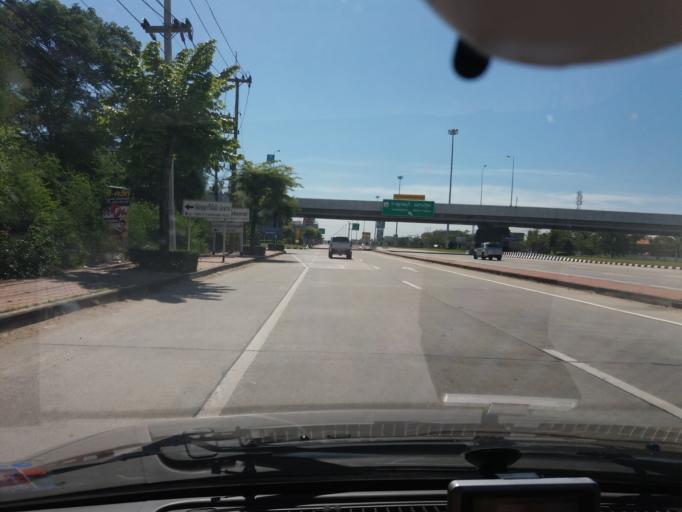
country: TH
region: Suphan Buri
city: Suphan Buri
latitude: 14.4661
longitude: 100.1317
